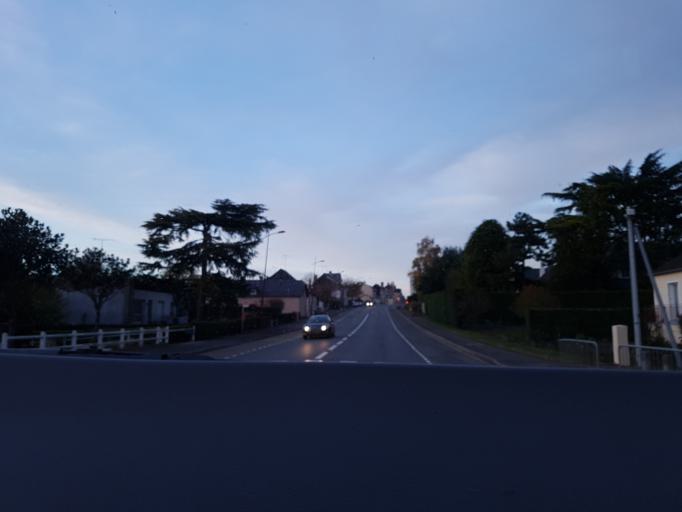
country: FR
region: Pays de la Loire
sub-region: Departement de la Mayenne
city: Cosse-le-Vivien
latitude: 47.9410
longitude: -0.9144
